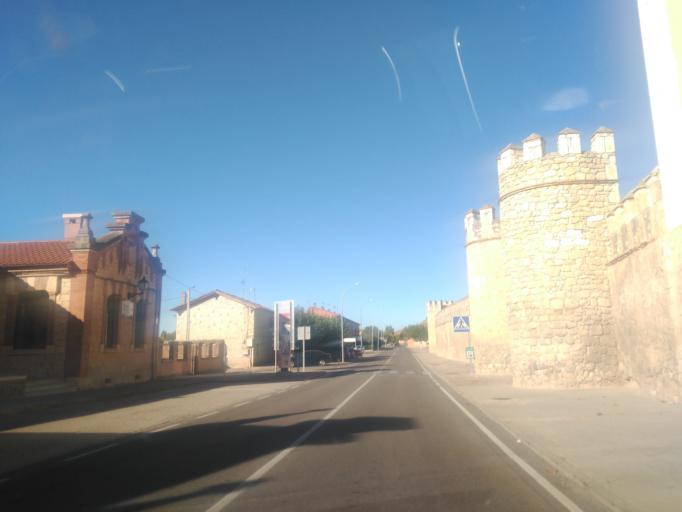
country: ES
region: Castille and Leon
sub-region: Provincia de Burgos
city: Penaranda de Duero
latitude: 41.6874
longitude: -3.4802
